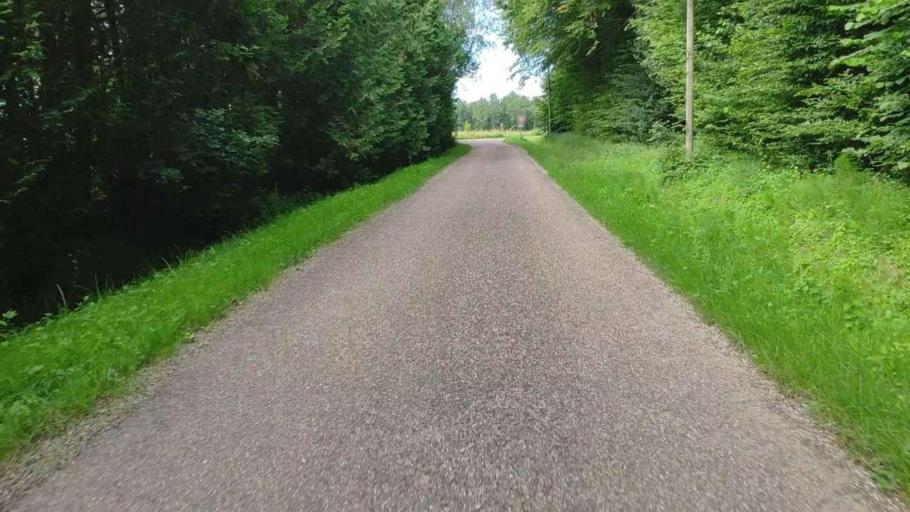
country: FR
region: Franche-Comte
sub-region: Departement du Jura
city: Bletterans
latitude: 46.8416
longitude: 5.5254
